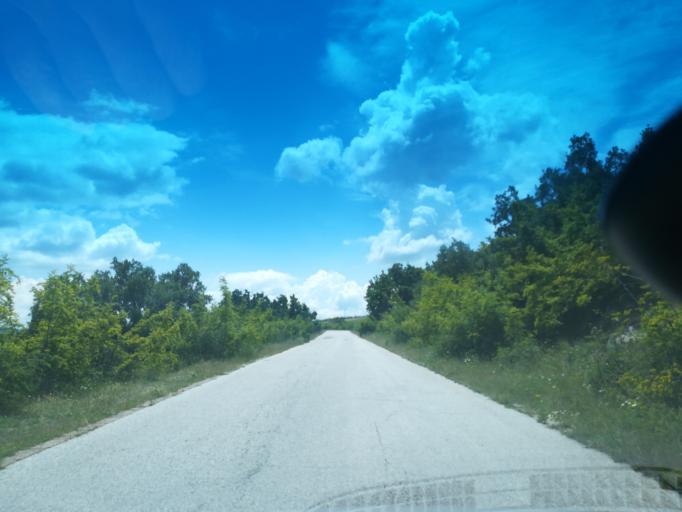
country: BG
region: Khaskovo
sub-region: Obshtina Mineralni Bani
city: Mineralni Bani
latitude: 41.9621
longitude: 25.2611
